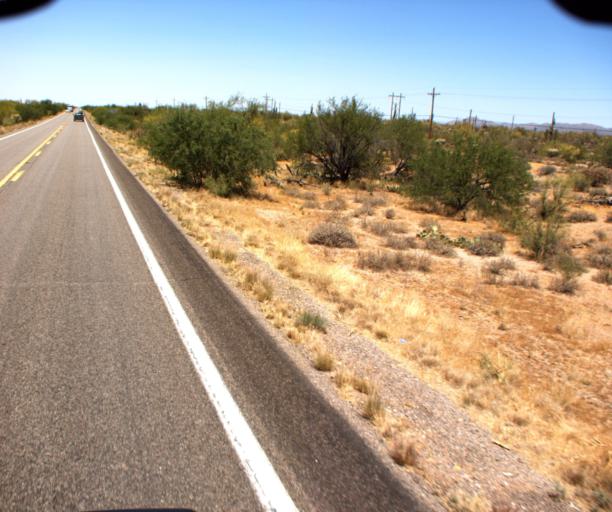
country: US
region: Arizona
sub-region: Pima County
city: Catalina
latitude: 32.7263
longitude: -111.1121
